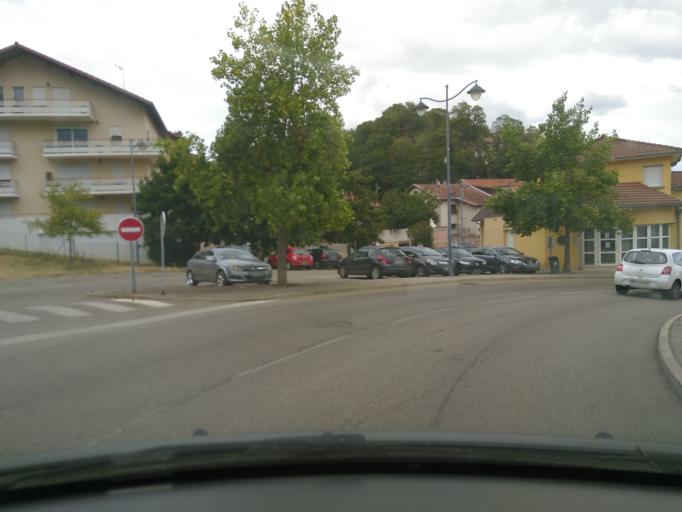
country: FR
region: Rhone-Alpes
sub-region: Departement de l'Isere
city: Beaurepaire
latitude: 45.3402
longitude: 5.0519
